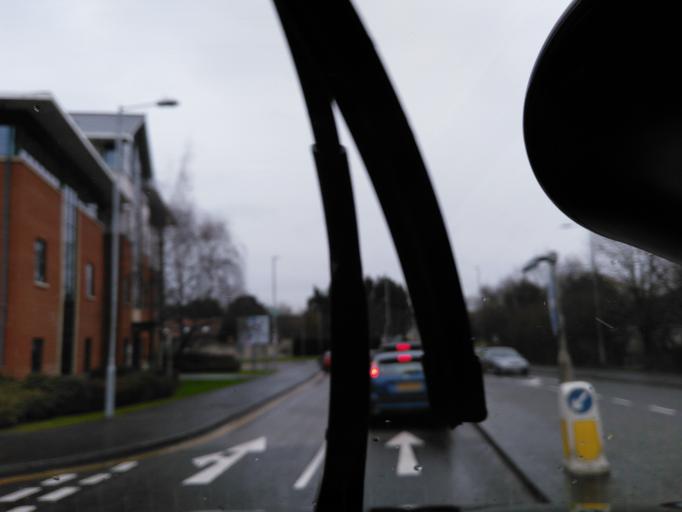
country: GB
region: England
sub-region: Wiltshire
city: Trowbridge
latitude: 51.3157
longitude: -2.2078
